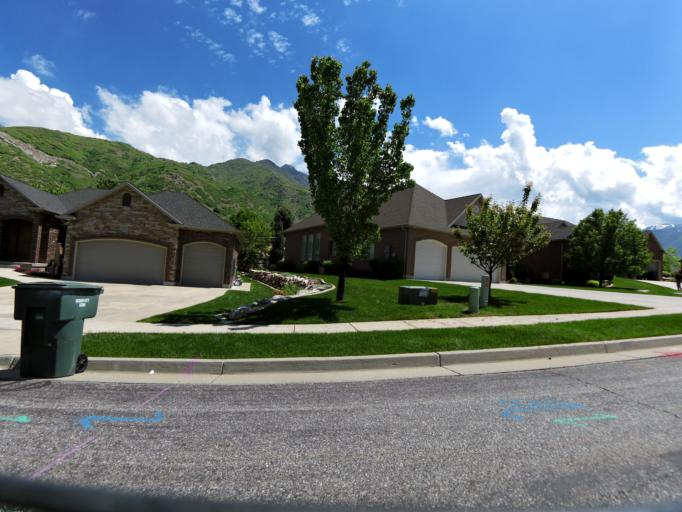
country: US
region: Utah
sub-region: Weber County
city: Uintah
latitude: 41.1629
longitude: -111.9261
